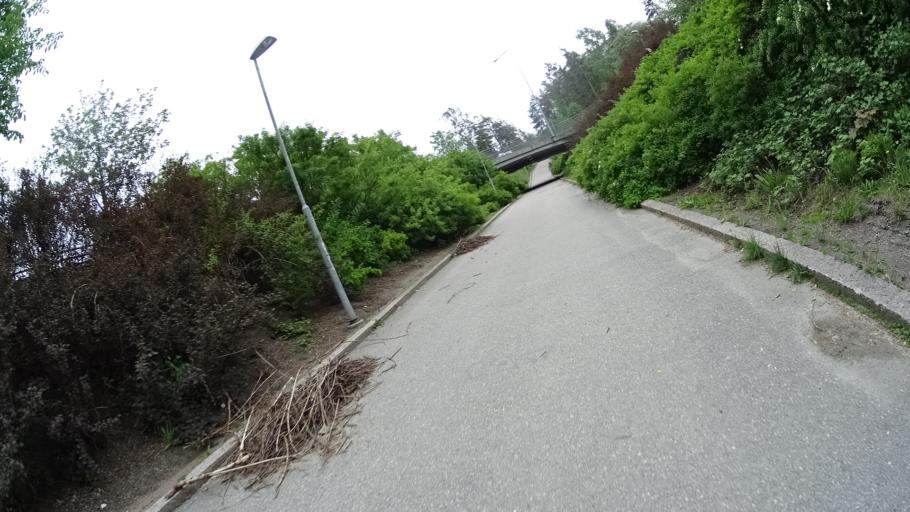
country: FI
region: Uusimaa
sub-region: Helsinki
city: Vantaa
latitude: 60.2425
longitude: 25.0744
